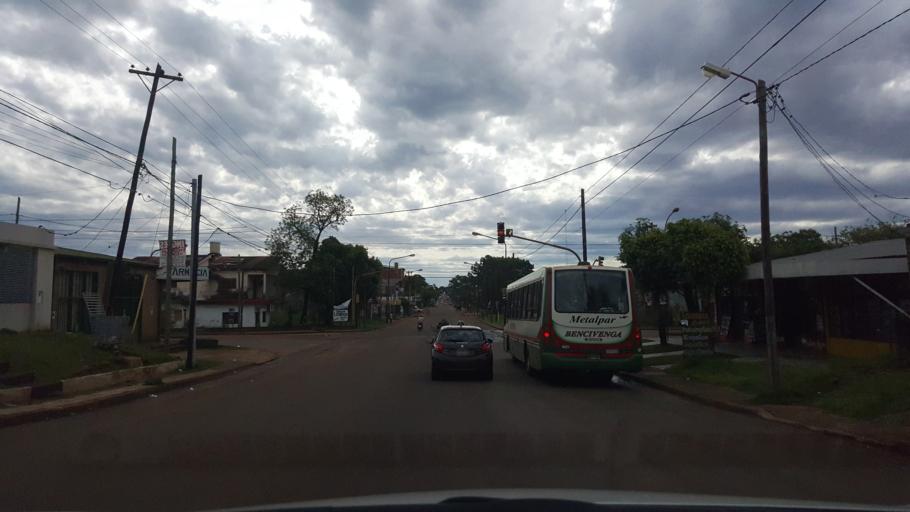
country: AR
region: Misiones
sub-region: Departamento de Capital
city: Posadas
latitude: -27.3707
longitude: -55.9316
